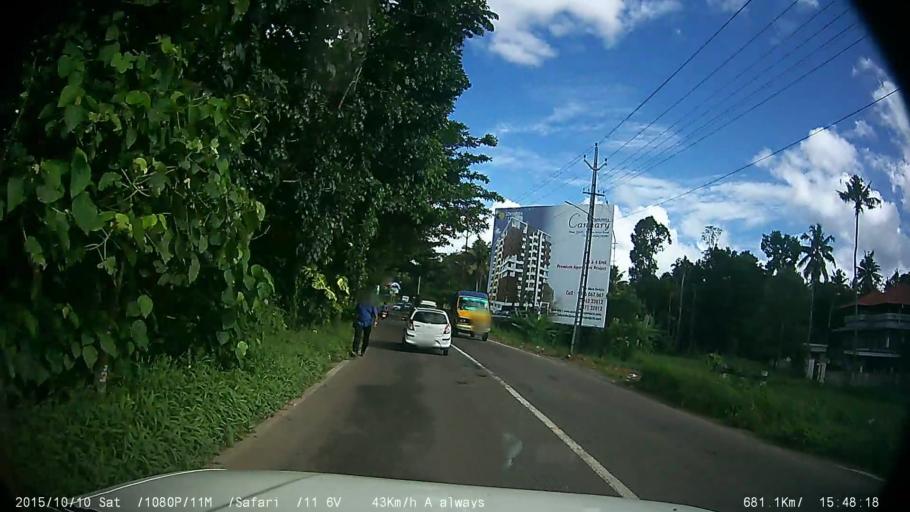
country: IN
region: Kerala
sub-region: Kottayam
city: Changanacheri
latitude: 9.4472
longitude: 76.5487
